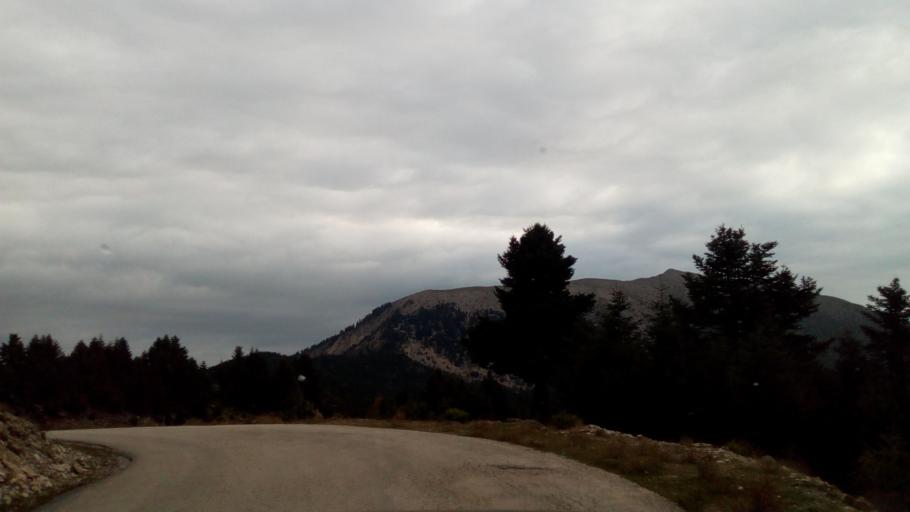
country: GR
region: West Greece
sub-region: Nomos Aitolias kai Akarnanias
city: Thermo
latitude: 38.6250
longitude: 21.8235
